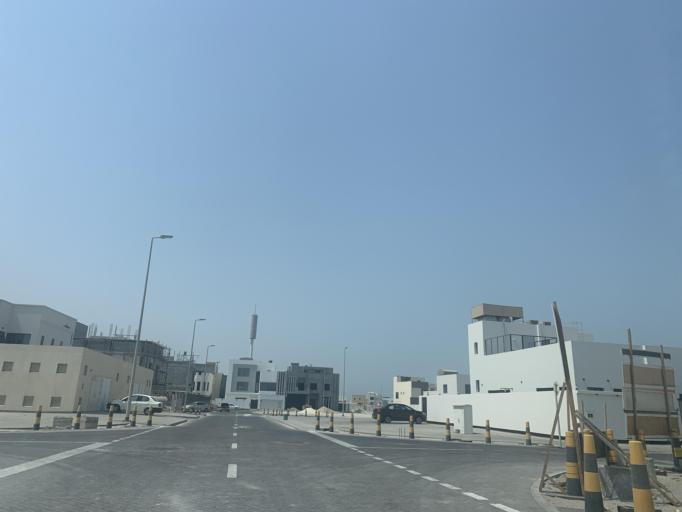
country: BH
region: Muharraq
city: Al Hadd
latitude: 26.2349
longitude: 50.6606
